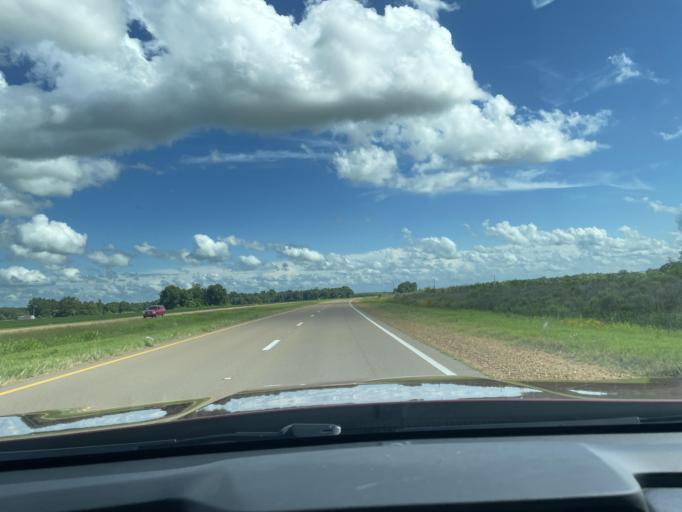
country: US
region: Mississippi
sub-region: Humphreys County
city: Belzoni
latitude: 33.0469
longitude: -90.4673
